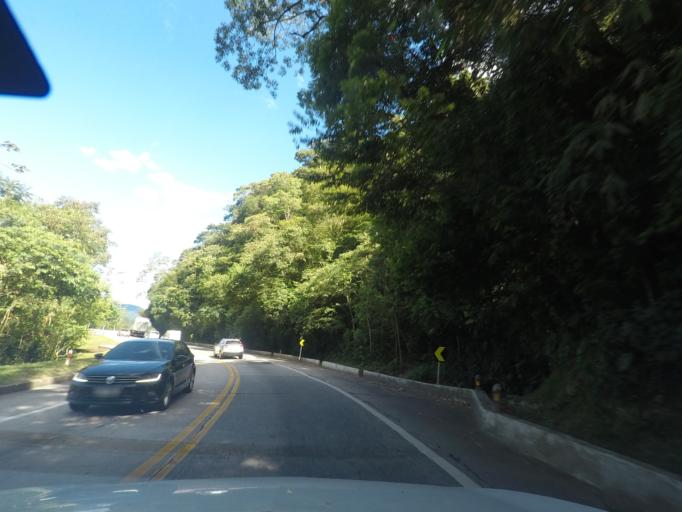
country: BR
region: Rio de Janeiro
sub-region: Teresopolis
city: Teresopolis
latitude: -22.4743
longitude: -43.0011
